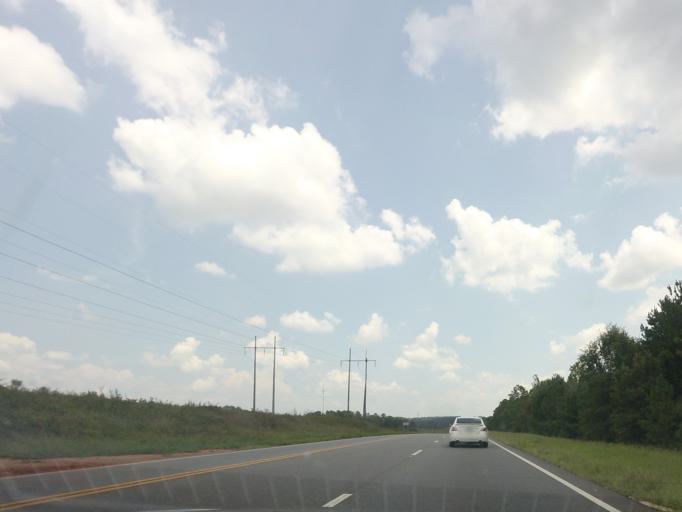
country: US
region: Georgia
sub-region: Houston County
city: Robins Air Force Base
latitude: 32.5408
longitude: -83.4777
